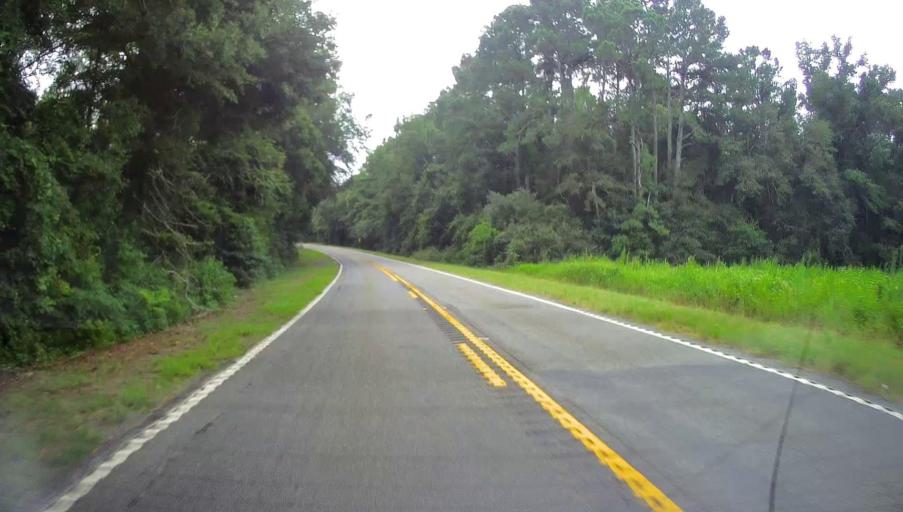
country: US
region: Georgia
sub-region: Dooly County
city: Unadilla
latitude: 32.2847
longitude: -83.8252
